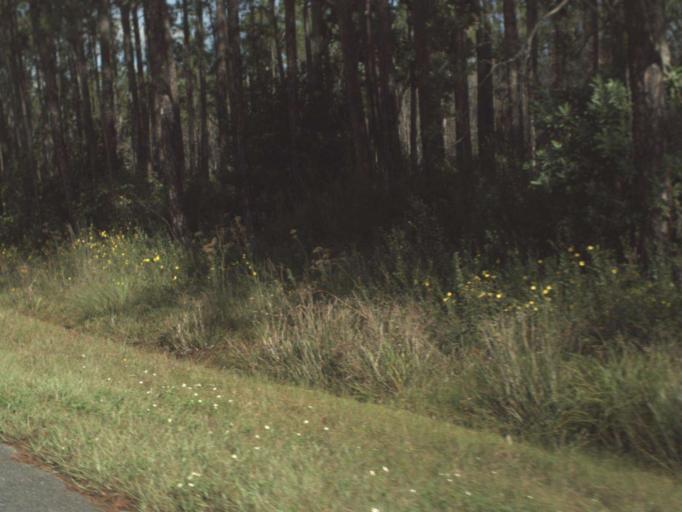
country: US
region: Florida
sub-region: Franklin County
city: Apalachicola
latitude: 29.8478
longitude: -84.9706
